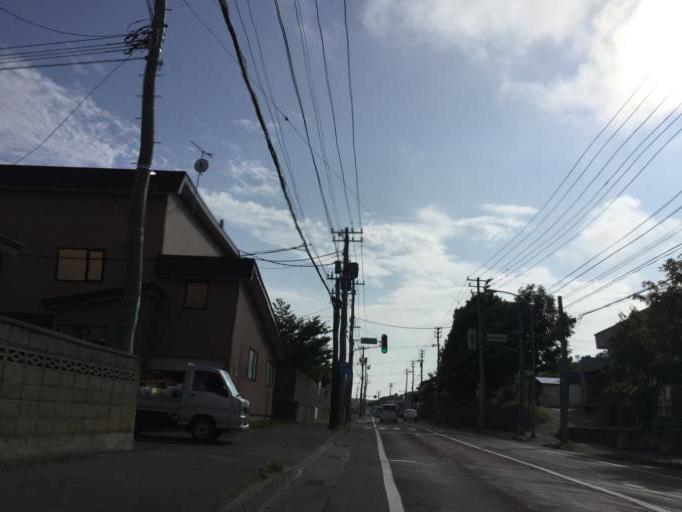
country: JP
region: Hokkaido
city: Wakkanai
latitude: 45.3900
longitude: 141.6793
